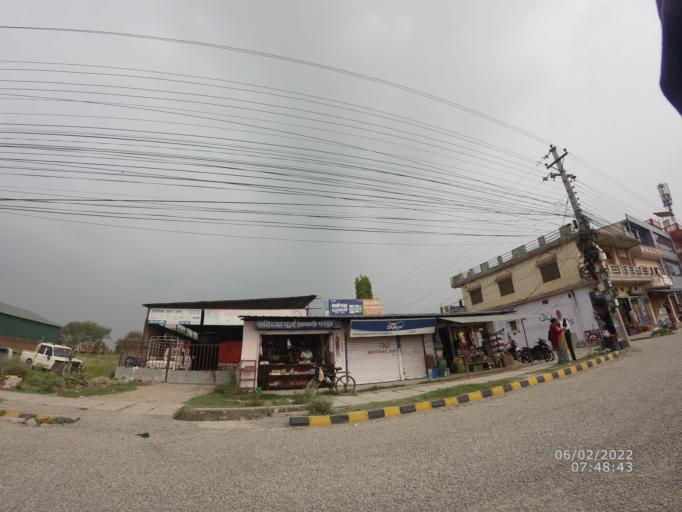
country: NP
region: Western Region
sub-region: Lumbini Zone
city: Bhairahawa
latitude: 27.5276
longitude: 83.4562
